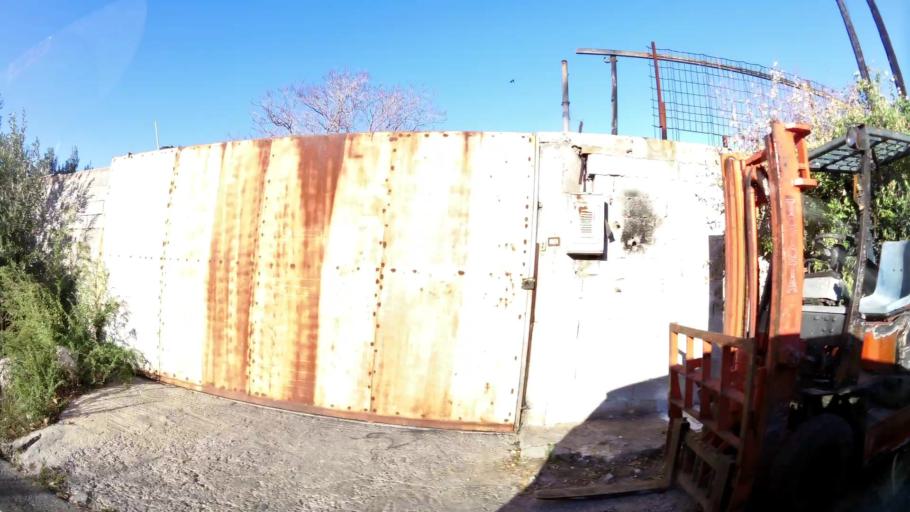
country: GR
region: Attica
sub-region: Nomarchia Athinas
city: Skaramangas
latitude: 38.0281
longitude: 23.6150
